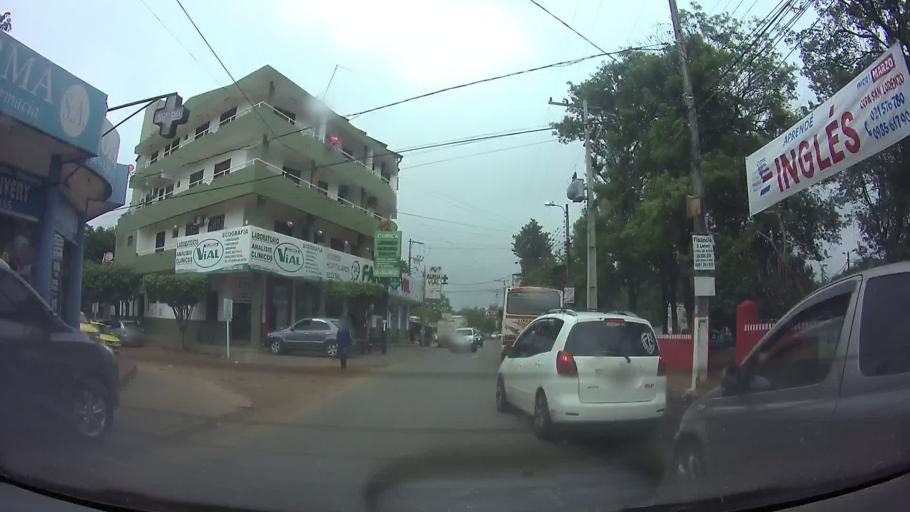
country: PY
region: Central
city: San Lorenzo
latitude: -25.3351
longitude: -57.5082
